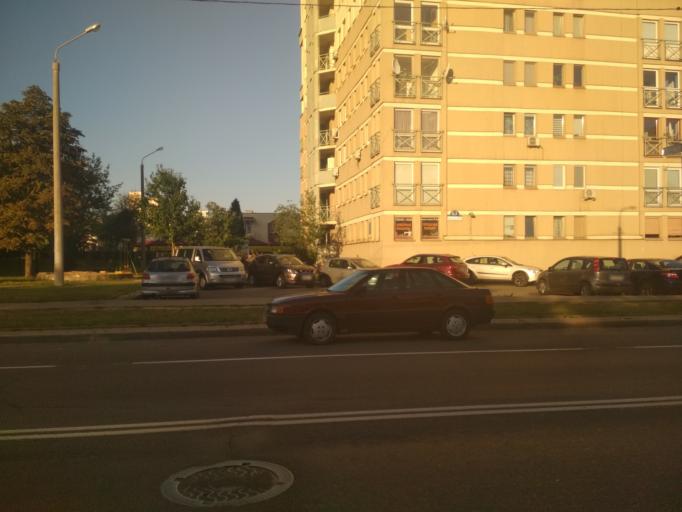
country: BY
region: Minsk
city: Minsk
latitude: 53.8983
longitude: 27.5868
